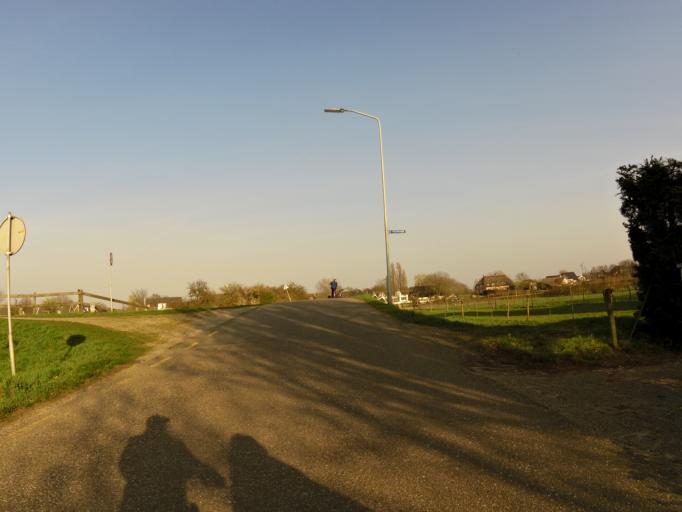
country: NL
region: North Brabant
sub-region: Gemeente Aalburg
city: Aalburg
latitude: 51.7821
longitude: 5.1190
